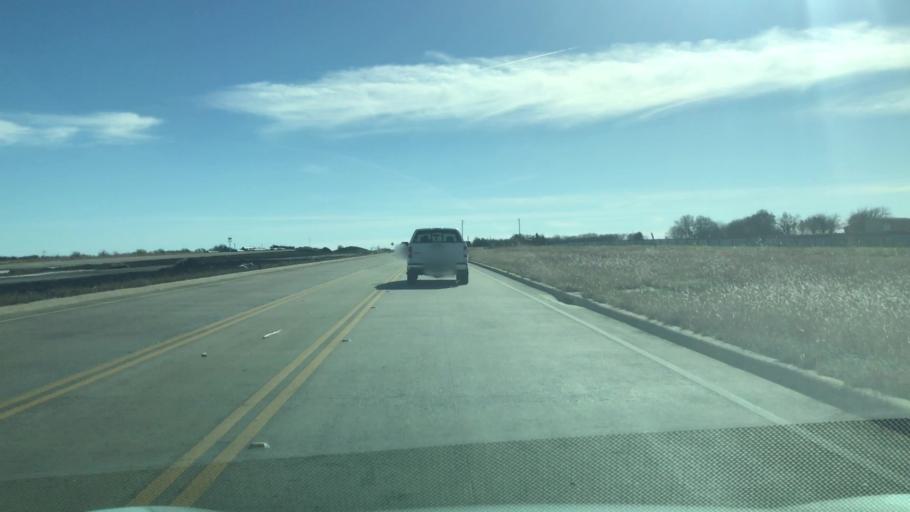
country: US
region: Texas
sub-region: Tarrant County
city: Mansfield
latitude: 32.5360
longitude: -97.0821
